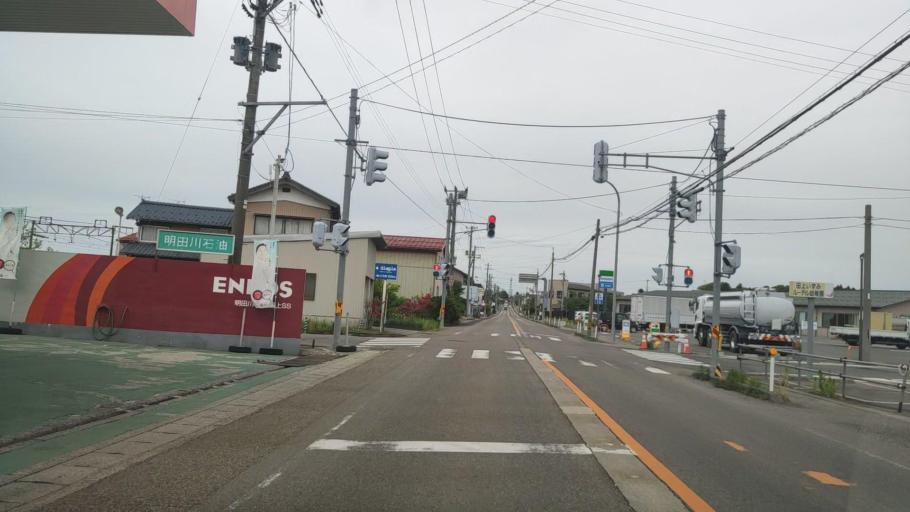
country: JP
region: Niigata
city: Kamo
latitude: 37.7197
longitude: 139.0756
